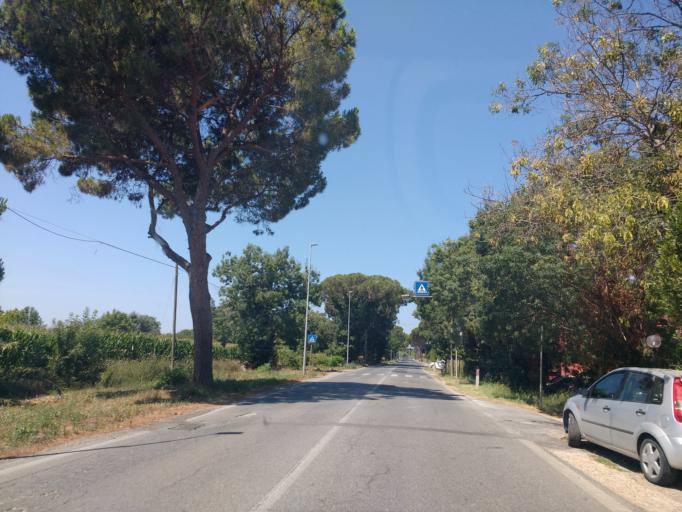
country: IT
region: Latium
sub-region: Citta metropolitana di Roma Capitale
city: Maccarese
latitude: 41.8783
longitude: 12.2067
